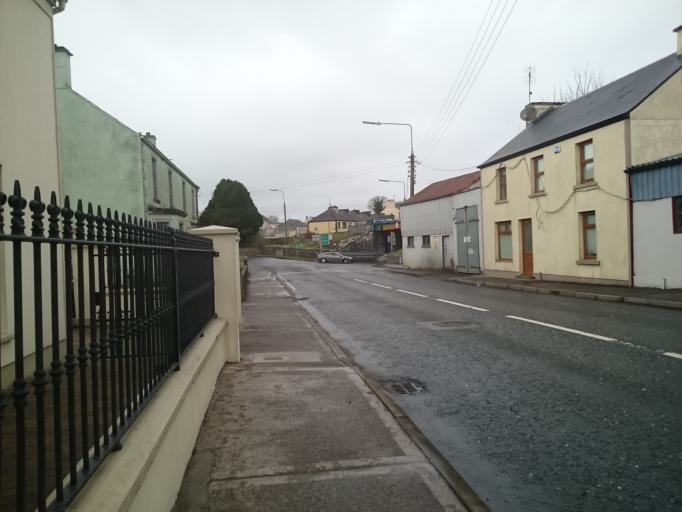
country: IE
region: Connaught
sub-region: Maigh Eo
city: Ballyhaunis
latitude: 53.7611
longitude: -8.7596
